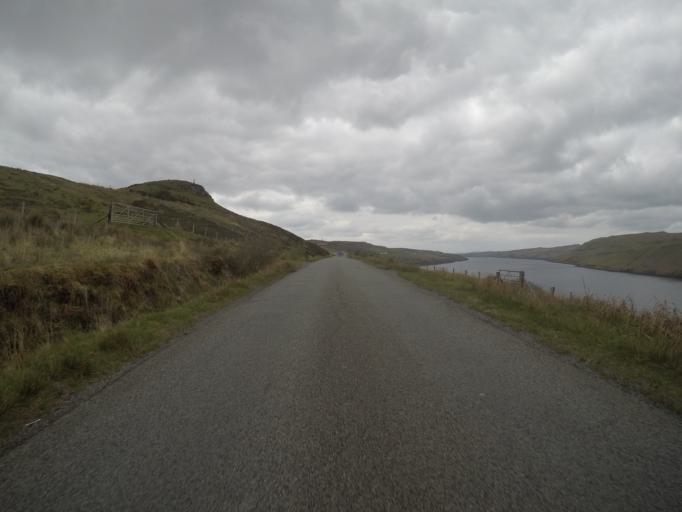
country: GB
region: Scotland
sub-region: Highland
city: Isle of Skye
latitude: 57.2963
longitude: -6.3412
